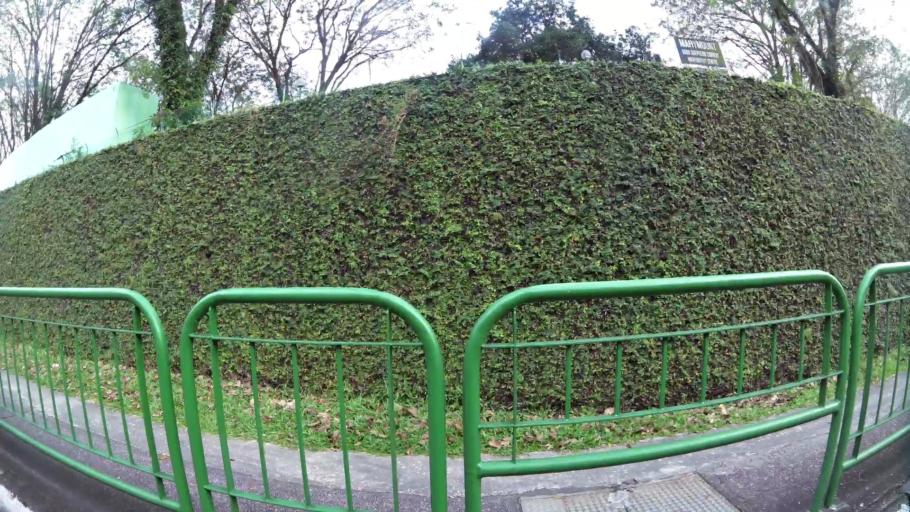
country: SG
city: Singapore
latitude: 1.3392
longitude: 103.8377
